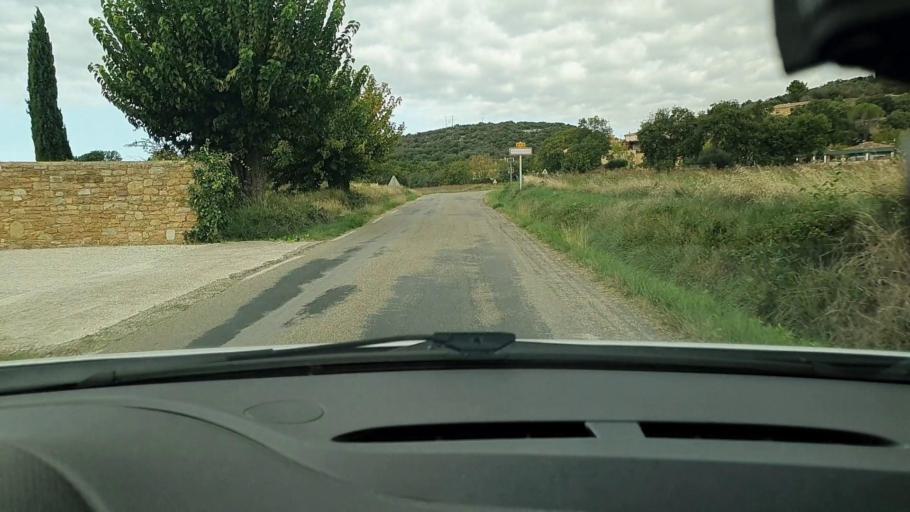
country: FR
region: Languedoc-Roussillon
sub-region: Departement du Gard
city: Montaren-et-Saint-Mediers
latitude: 44.0571
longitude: 4.3233
